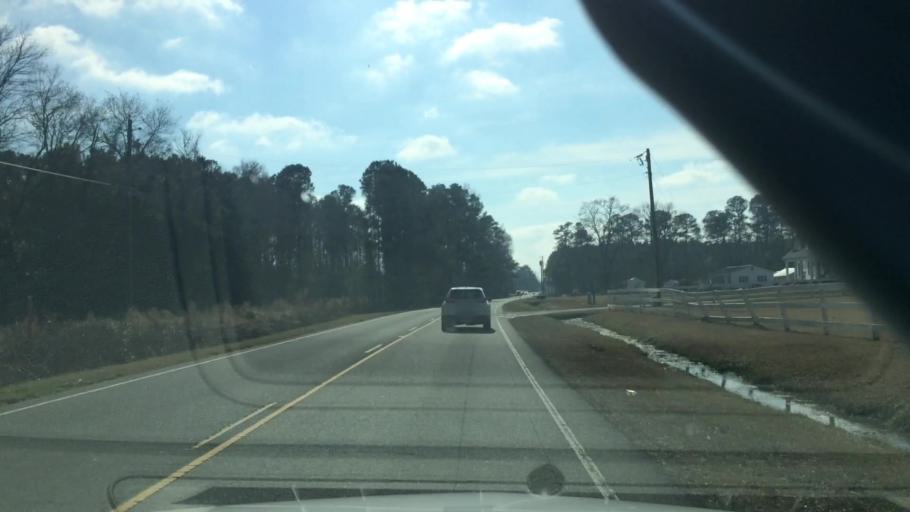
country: US
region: North Carolina
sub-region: Duplin County
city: Beulaville
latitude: 34.8696
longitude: -77.7921
